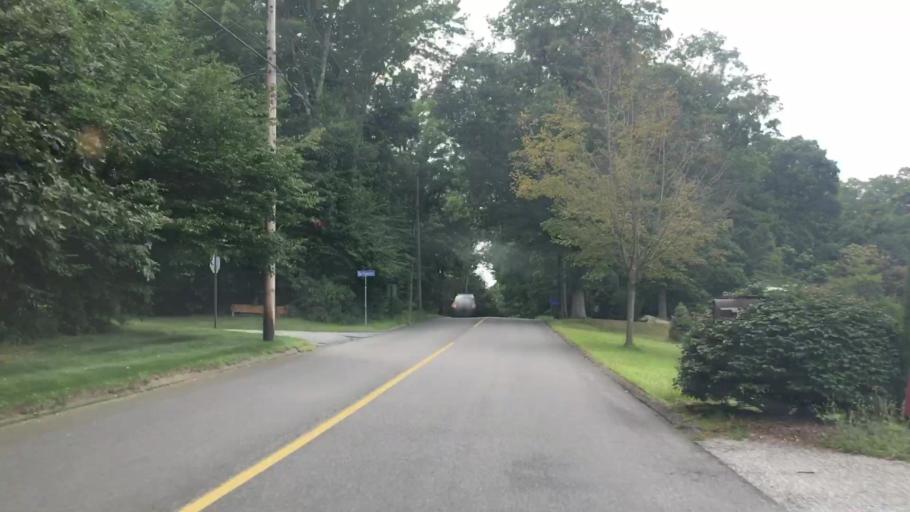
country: US
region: Connecticut
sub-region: Middlesex County
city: Deep River Center
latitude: 41.3378
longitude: -72.4360
